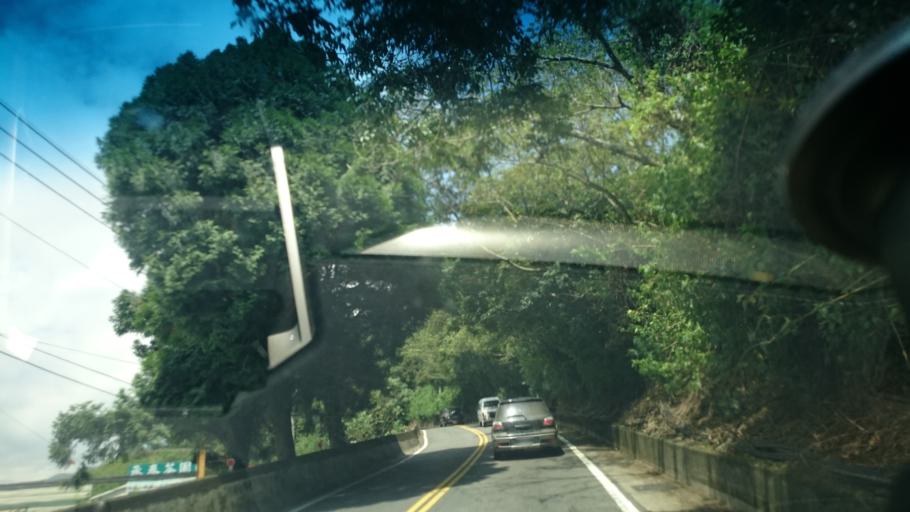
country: TW
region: Taiwan
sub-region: Nantou
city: Puli
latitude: 24.0354
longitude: 121.1434
